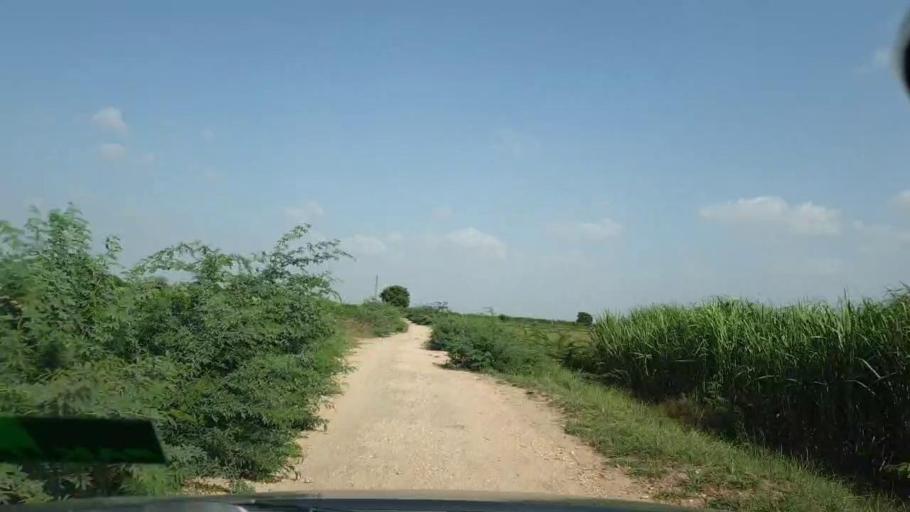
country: PK
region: Sindh
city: Tando Bago
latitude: 24.6827
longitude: 69.2018
